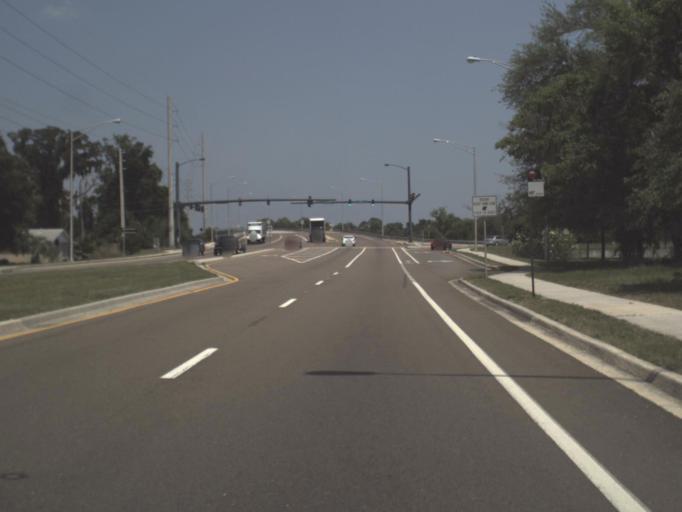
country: US
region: Florida
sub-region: Duval County
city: Atlantic Beach
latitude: 30.3582
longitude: -81.4644
